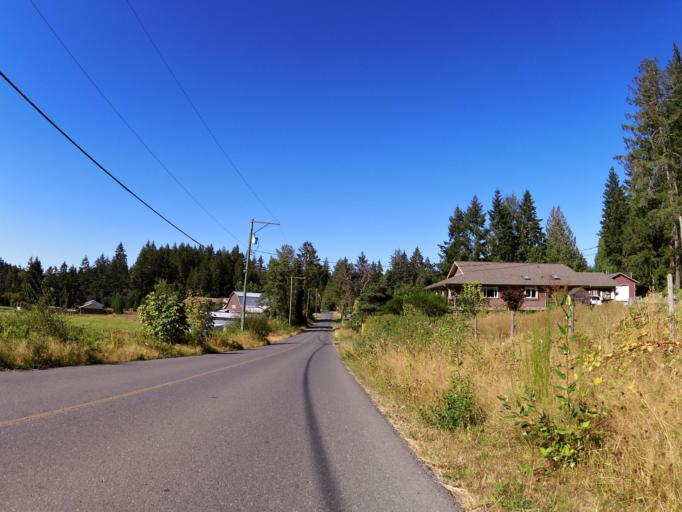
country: CA
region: British Columbia
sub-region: Cowichan Valley Regional District
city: Ladysmith
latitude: 49.0396
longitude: -123.8505
